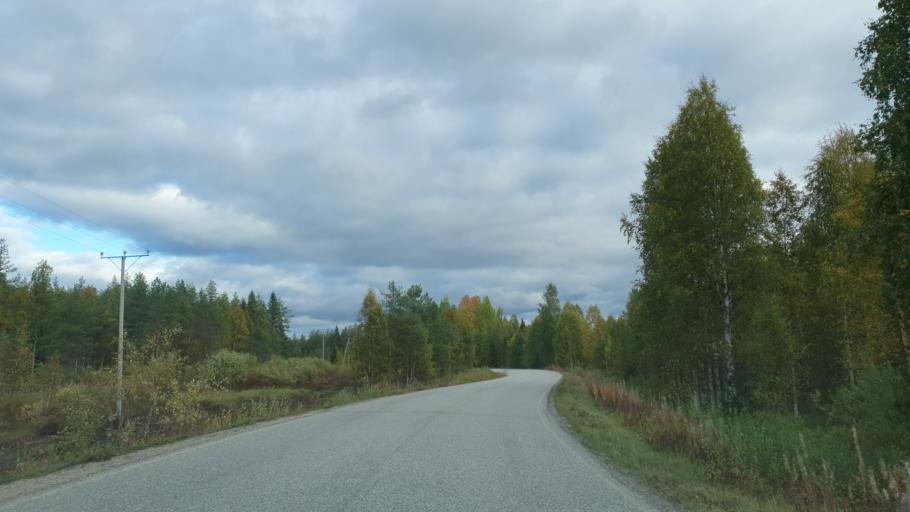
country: FI
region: Kainuu
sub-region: Kehys-Kainuu
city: Kuhmo
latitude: 63.9488
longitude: 29.8764
